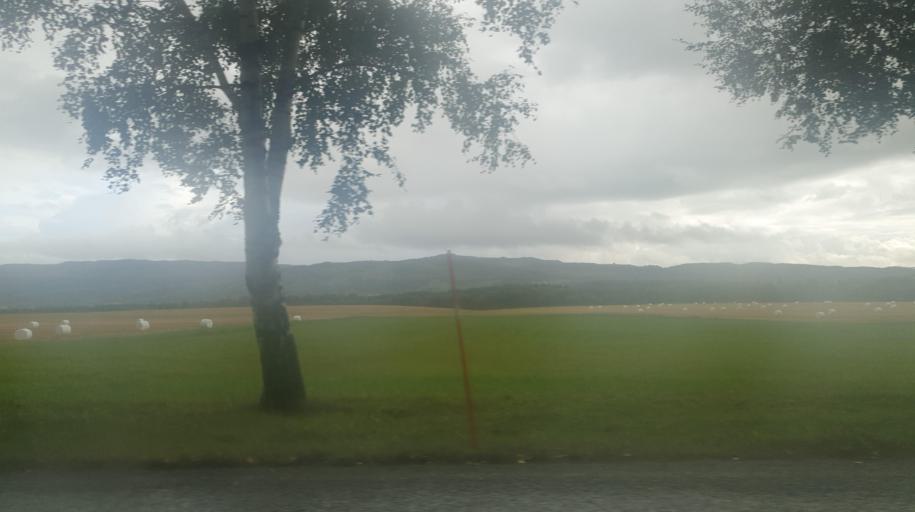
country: NO
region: Nord-Trondelag
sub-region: Verdal
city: Verdal
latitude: 63.7943
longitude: 11.5443
